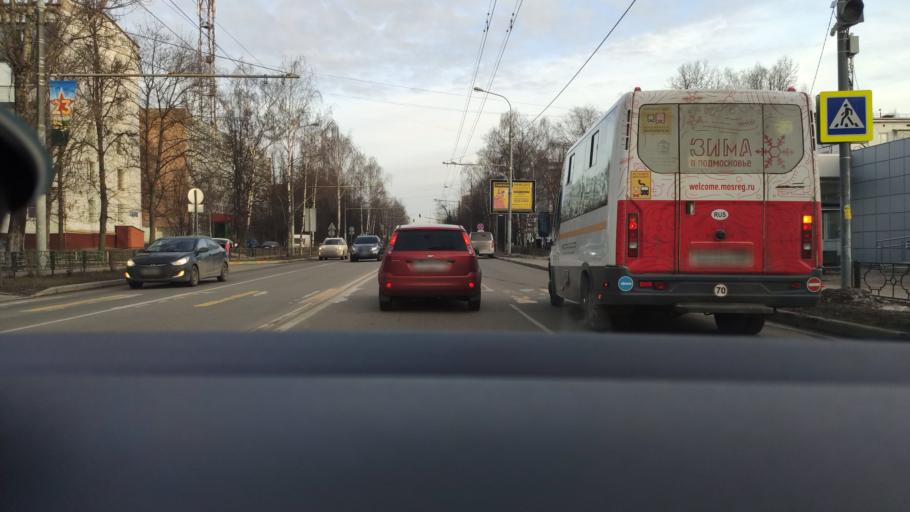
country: RU
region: Moskovskaya
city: Vidnoye
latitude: 55.5503
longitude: 37.7104
